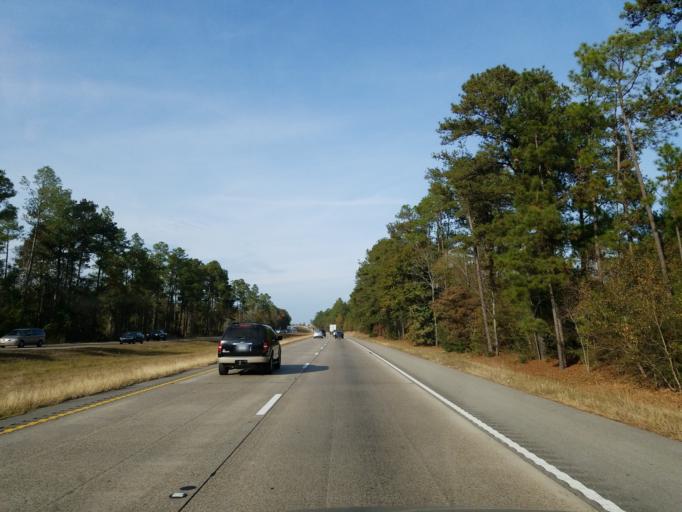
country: US
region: Mississippi
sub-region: Forrest County
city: Glendale
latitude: 31.4197
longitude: -89.3180
